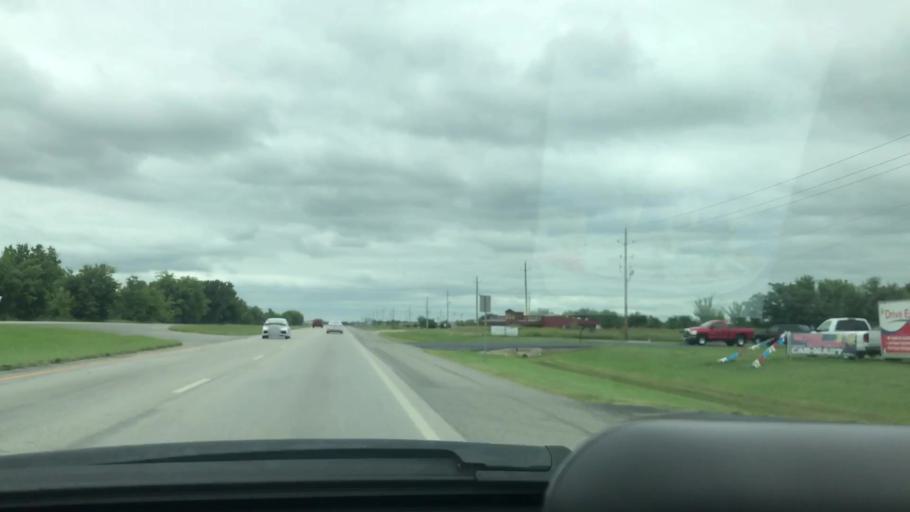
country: US
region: Oklahoma
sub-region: Mayes County
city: Pryor
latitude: 36.2533
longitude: -95.3350
